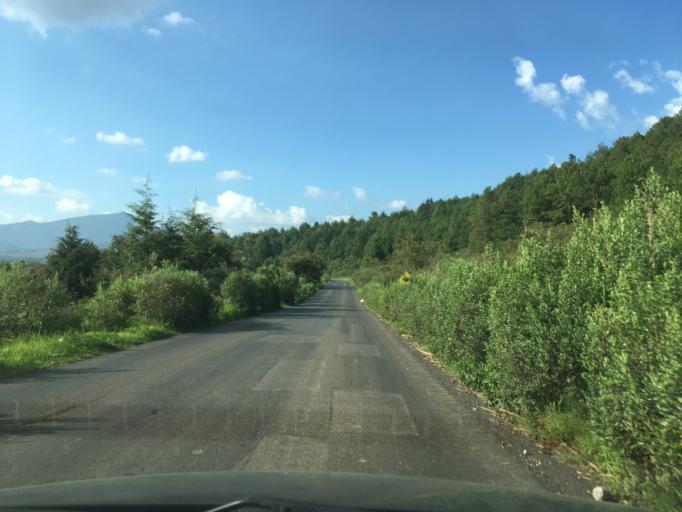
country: MX
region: Michoacan
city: Nahuatzen
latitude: 19.6342
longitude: -101.9269
